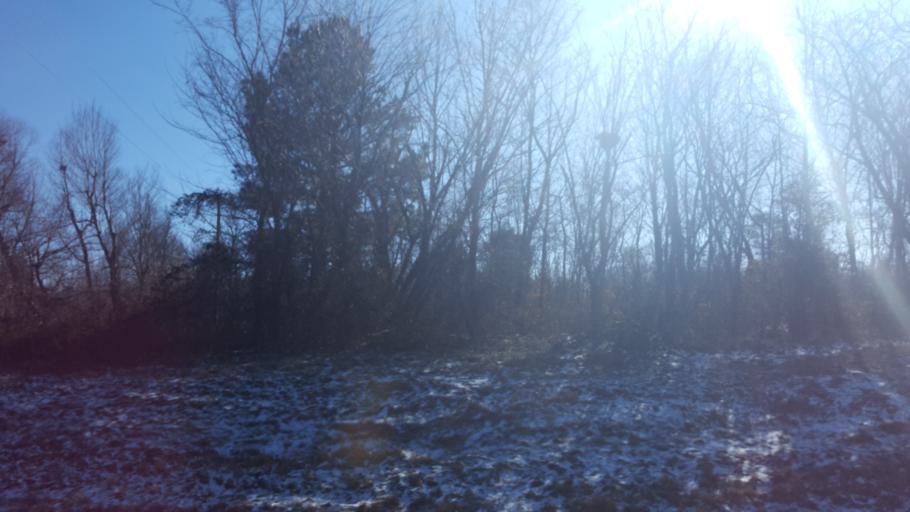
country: US
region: Kentucky
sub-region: Crittenden County
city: Marion
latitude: 37.3661
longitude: -88.0390
